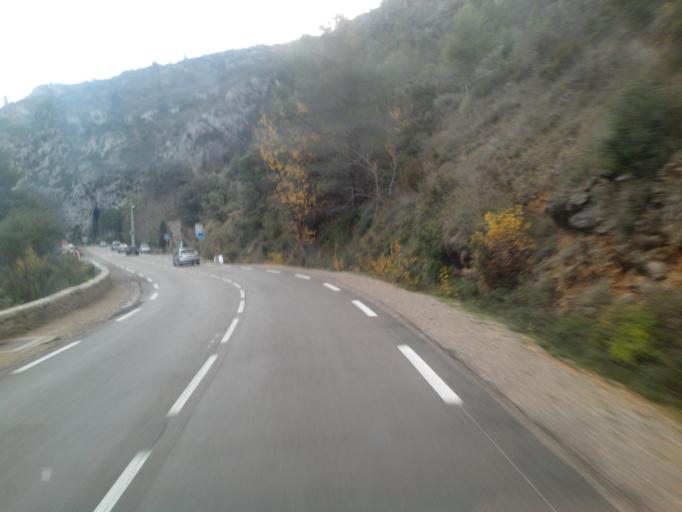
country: FR
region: Languedoc-Roussillon
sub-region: Departement de l'Herault
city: Saint-Jean-de-Fos
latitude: 43.7118
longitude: 3.5523
